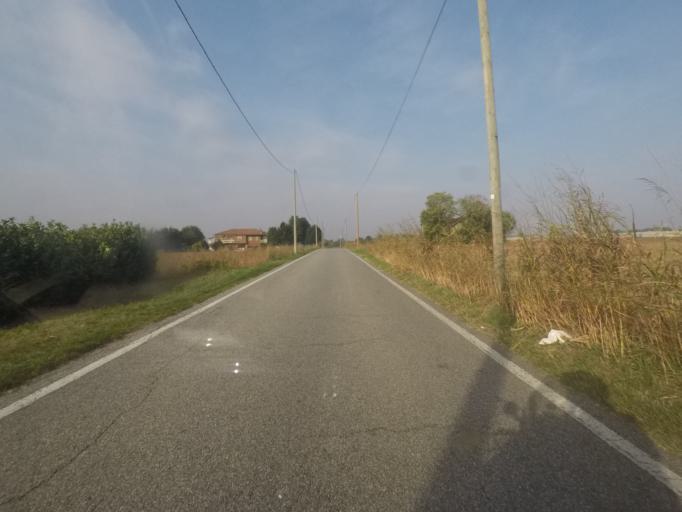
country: IT
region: Lombardy
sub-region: Provincia di Monza e Brianza
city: Bellusco
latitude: 45.6270
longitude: 9.4036
